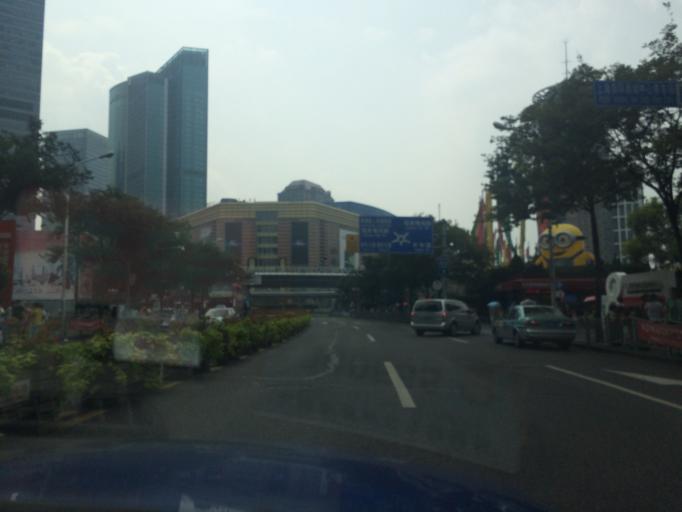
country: CN
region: Shanghai Shi
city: Hongkou
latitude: 31.2416
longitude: 121.4970
